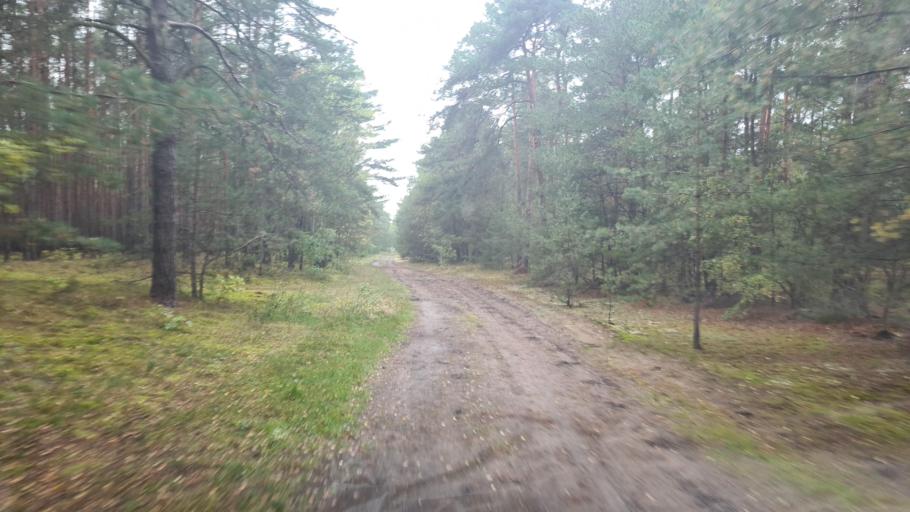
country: DE
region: Brandenburg
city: Storkow
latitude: 52.2243
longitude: 13.9125
